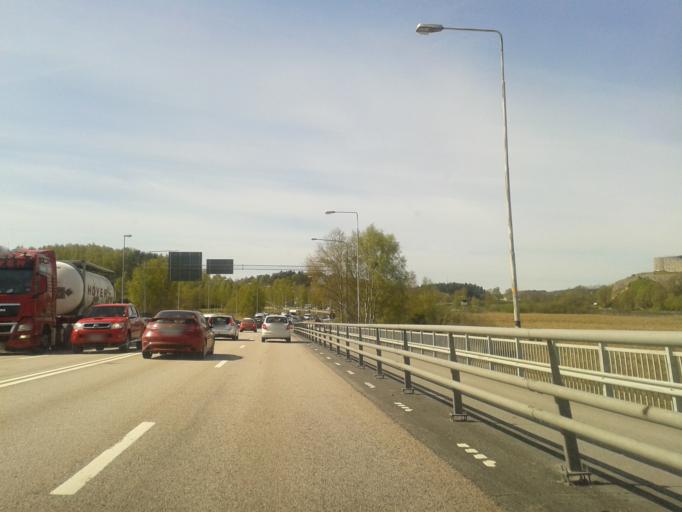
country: SE
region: Vaestra Goetaland
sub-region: Kungalvs Kommun
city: Kungalv
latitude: 57.8561
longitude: 12.0055
